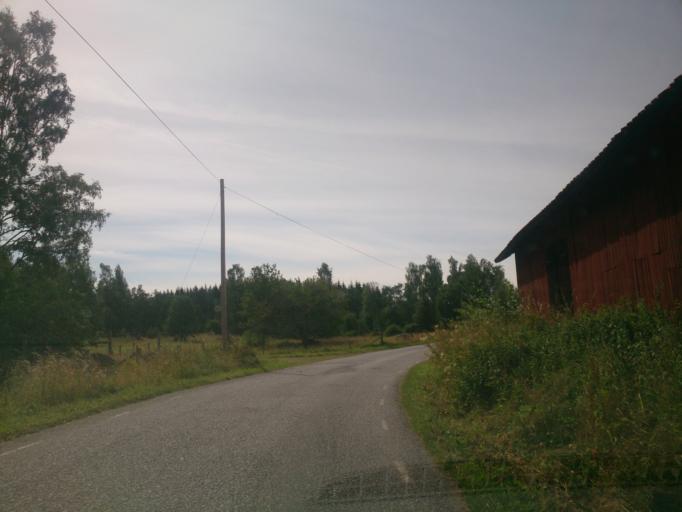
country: SE
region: OEstergoetland
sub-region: Atvidabergs Kommun
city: Atvidaberg
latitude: 58.2975
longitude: 16.0963
